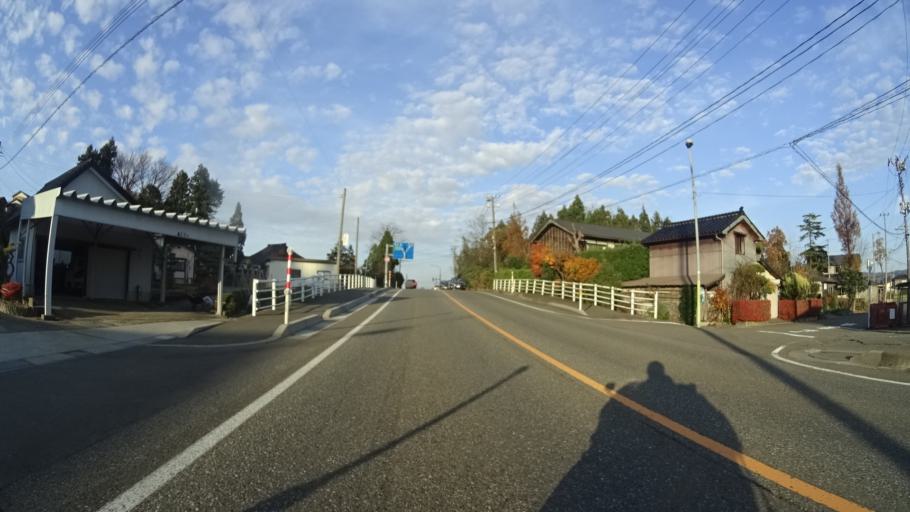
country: JP
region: Niigata
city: Kashiwazaki
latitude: 37.3952
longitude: 138.6029
